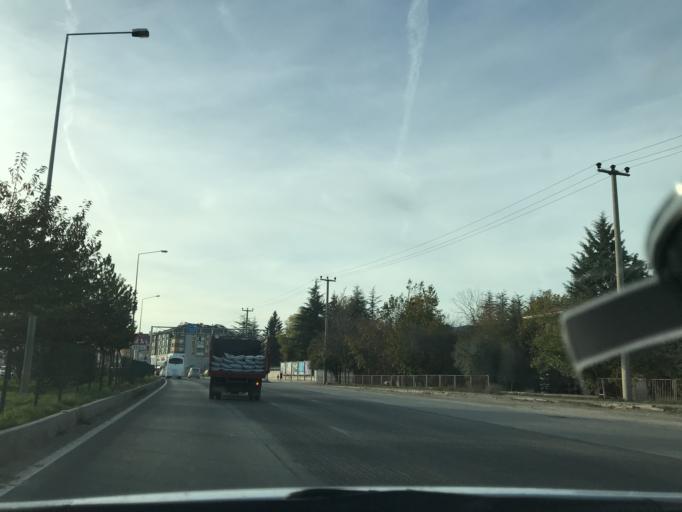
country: TR
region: Bolu
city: Bolu
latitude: 40.7387
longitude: 31.6121
